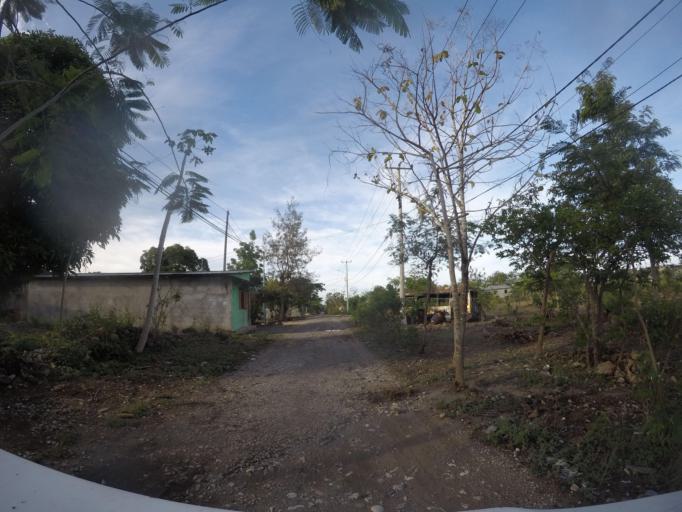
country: TL
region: Baucau
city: Baucau
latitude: -8.4877
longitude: 126.4523
